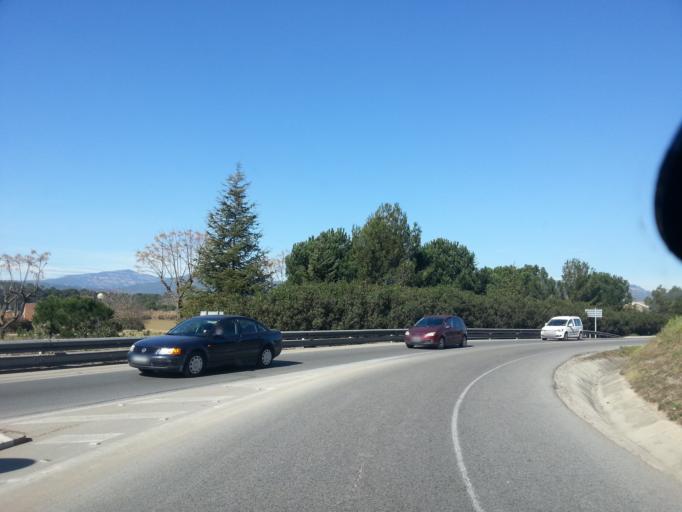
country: ES
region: Catalonia
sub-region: Provincia de Barcelona
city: Caldes de Montbui
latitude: 41.5991
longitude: 2.1806
